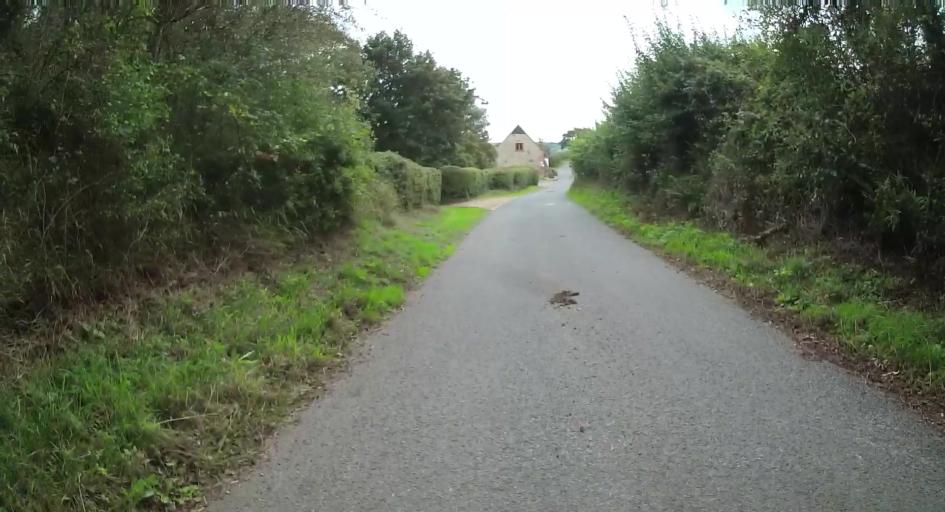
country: GB
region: England
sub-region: Isle of Wight
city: Niton
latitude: 50.6377
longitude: -1.2722
